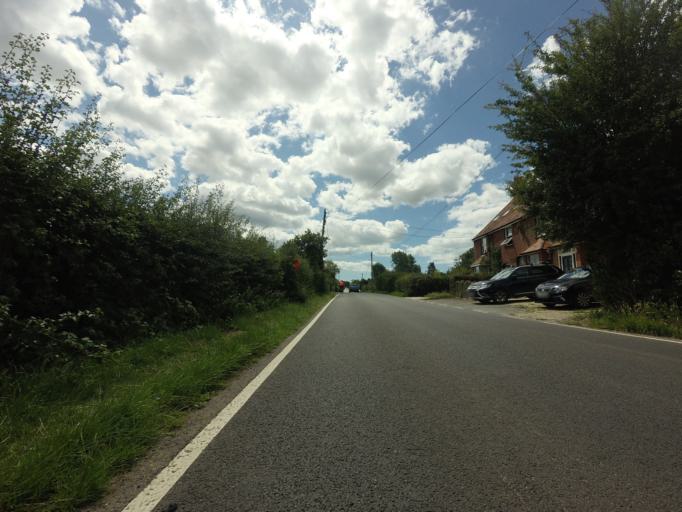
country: GB
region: England
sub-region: East Sussex
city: Hailsham
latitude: 50.8443
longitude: 0.1678
